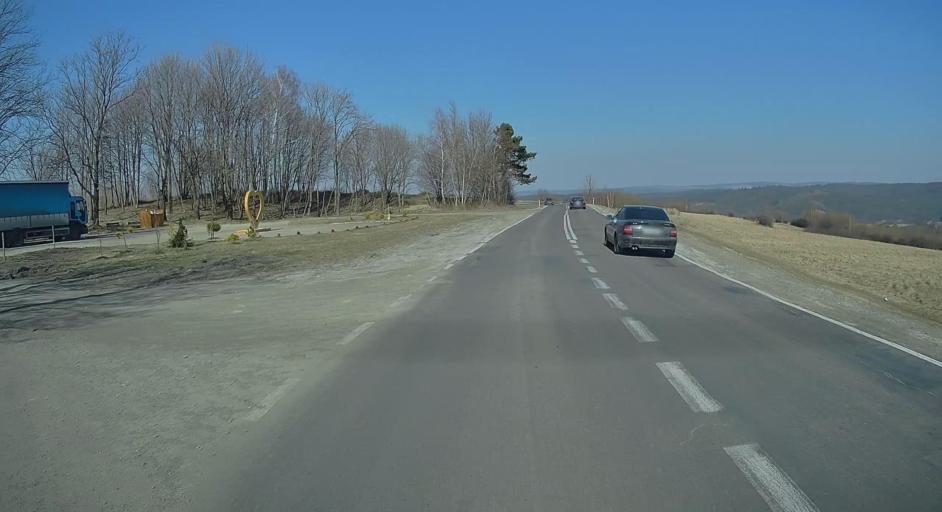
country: PL
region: Subcarpathian Voivodeship
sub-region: Powiat przemyski
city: Bircza
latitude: 49.6411
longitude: 22.4233
